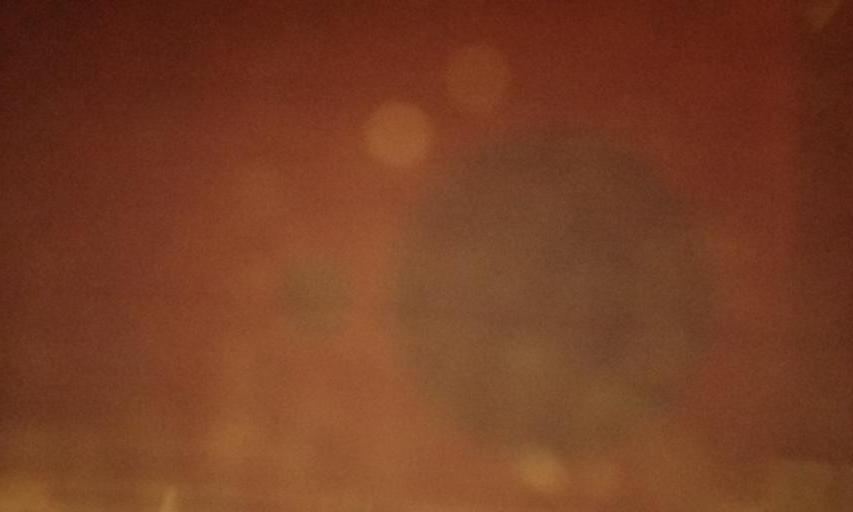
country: JP
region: Okayama
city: Kamogatacho-kamogata
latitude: 34.5354
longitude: 133.5510
